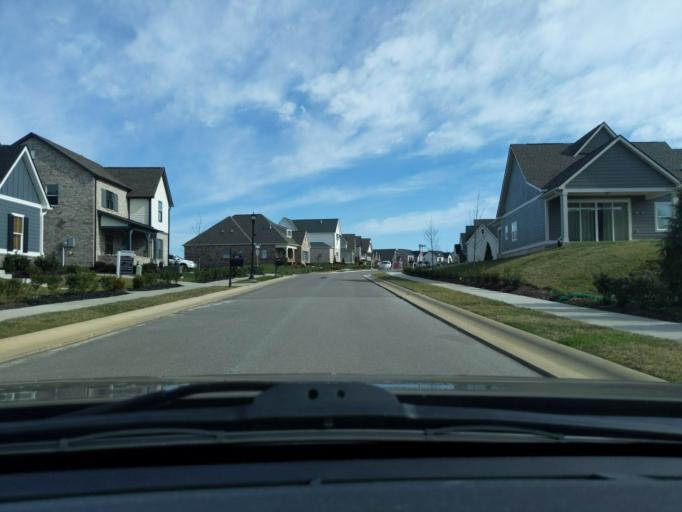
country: US
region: Tennessee
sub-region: Wilson County
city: Mount Juliet
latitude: 36.2113
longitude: -86.4922
